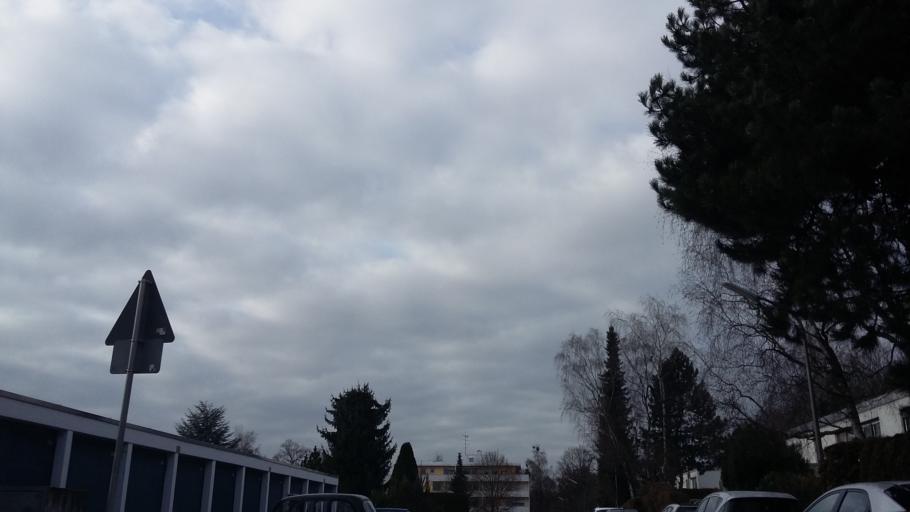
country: DE
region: Bavaria
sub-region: Upper Bavaria
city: Grafelfing
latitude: 48.1267
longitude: 11.4408
